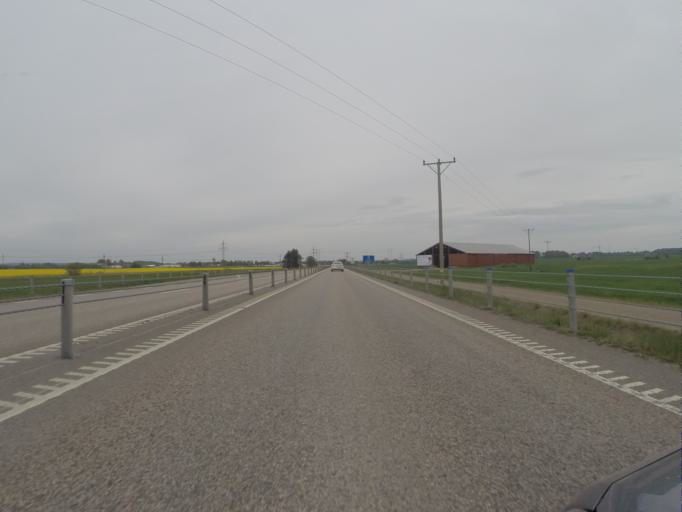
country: SE
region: Skane
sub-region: Helsingborg
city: Morarp
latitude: 56.0870
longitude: 12.8768
